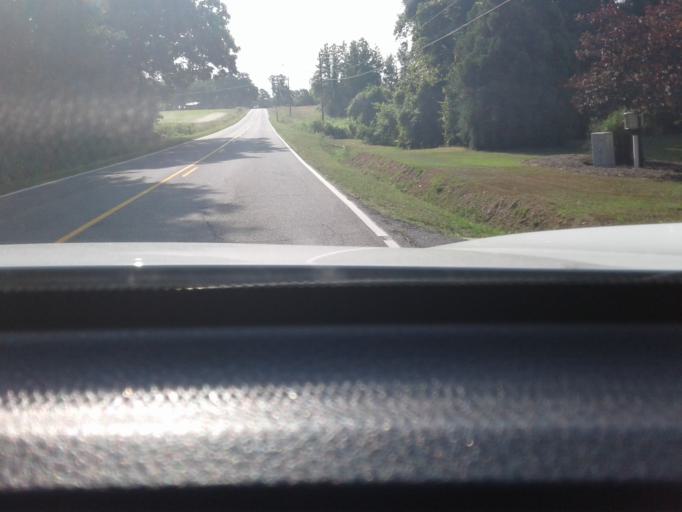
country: US
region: North Carolina
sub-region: Johnston County
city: Benson
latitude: 35.3876
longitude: -78.5634
